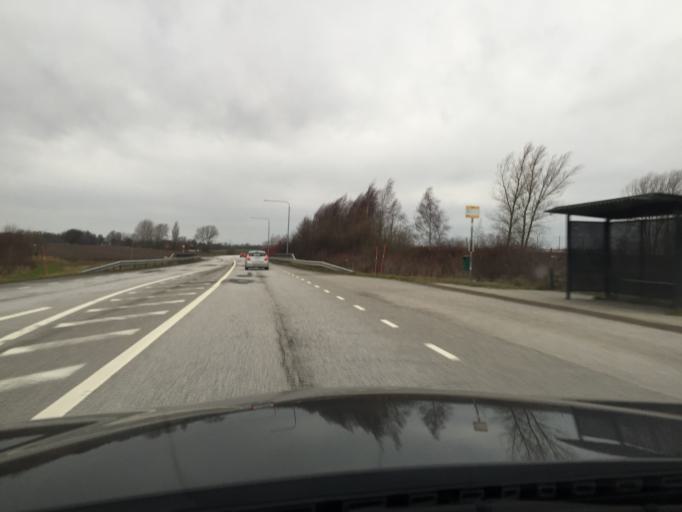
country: SE
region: Skane
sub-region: Malmo
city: Oxie
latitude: 55.5838
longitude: 13.1335
